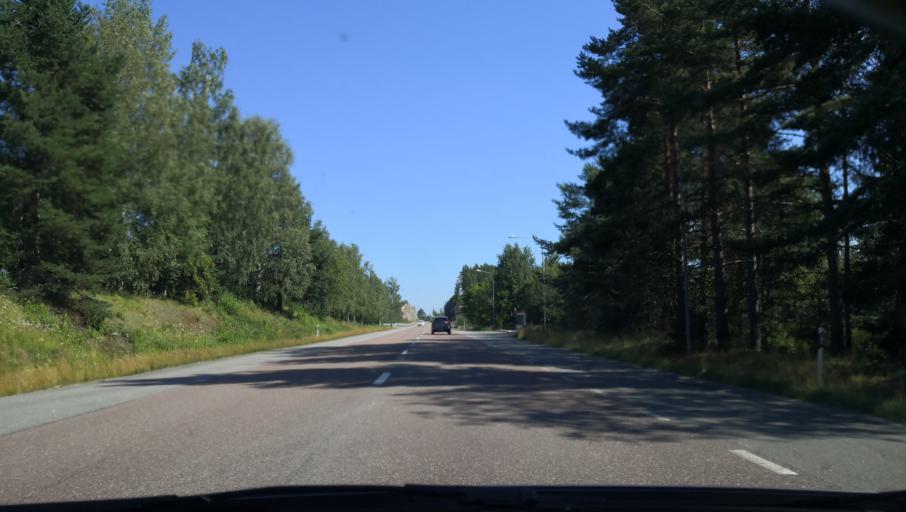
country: SE
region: Gaevleborg
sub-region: Bollnas Kommun
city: Bollnas
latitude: 61.3300
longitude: 16.2475
